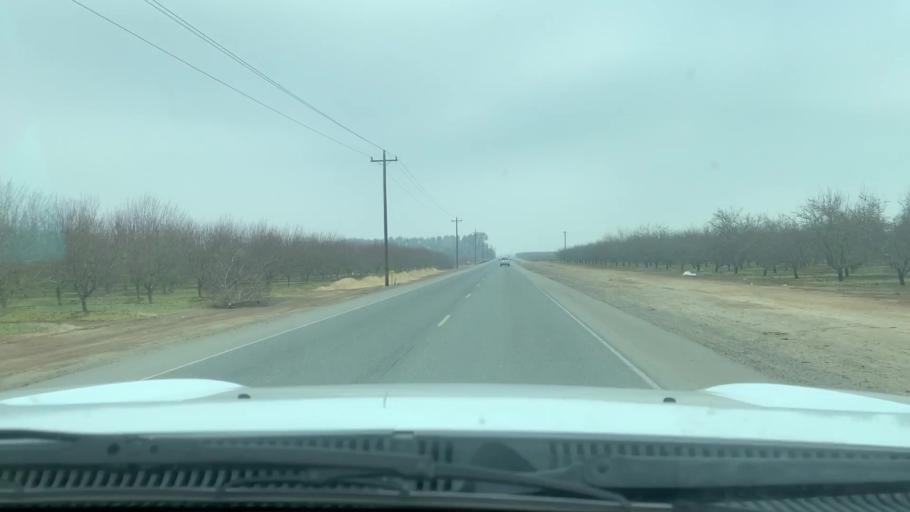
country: US
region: California
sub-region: Kern County
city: Buttonwillow
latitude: 35.5006
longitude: -119.4866
